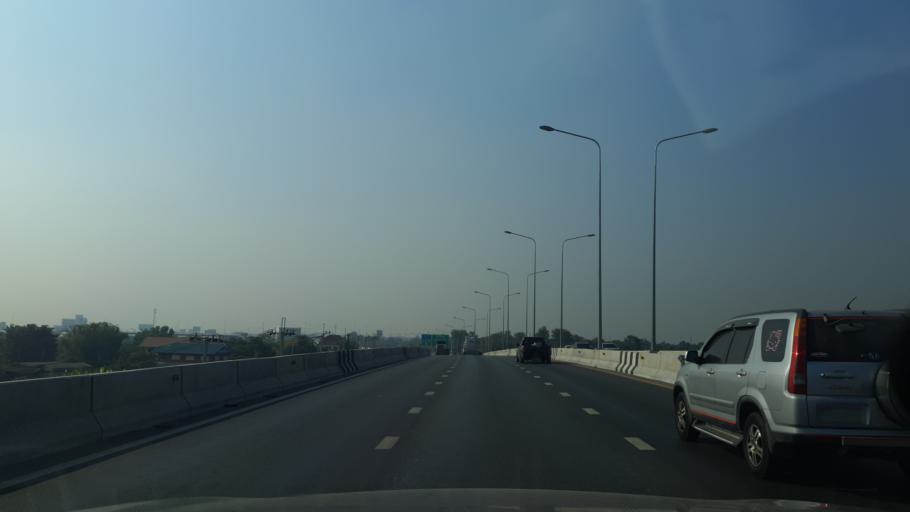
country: TH
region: Nonthaburi
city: Bang Bua Thong
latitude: 13.9618
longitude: 100.4598
